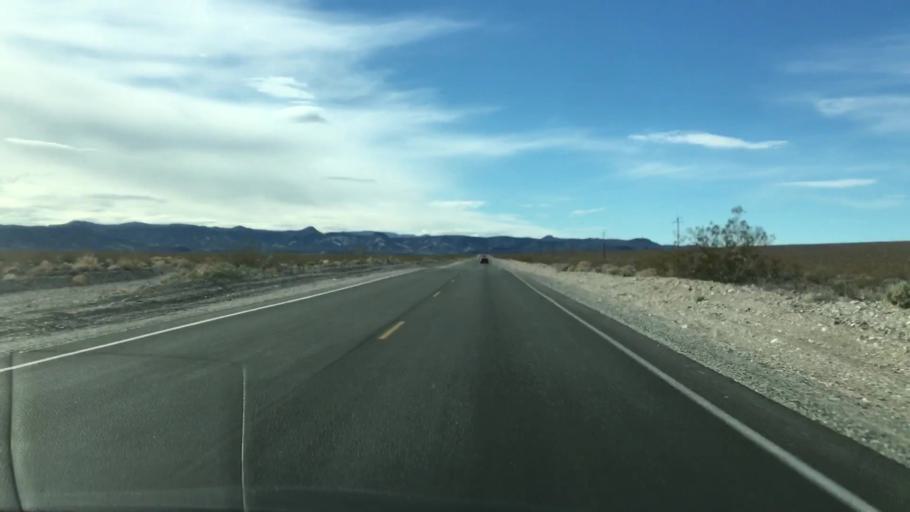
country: US
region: Nevada
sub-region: Nye County
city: Pahrump
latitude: 36.3033
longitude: -116.4840
